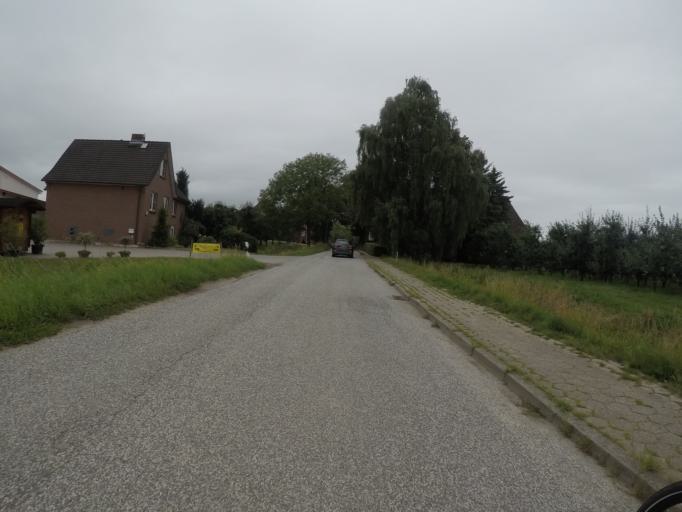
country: DE
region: Hamburg
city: Altona
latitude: 53.5279
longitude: 9.8553
